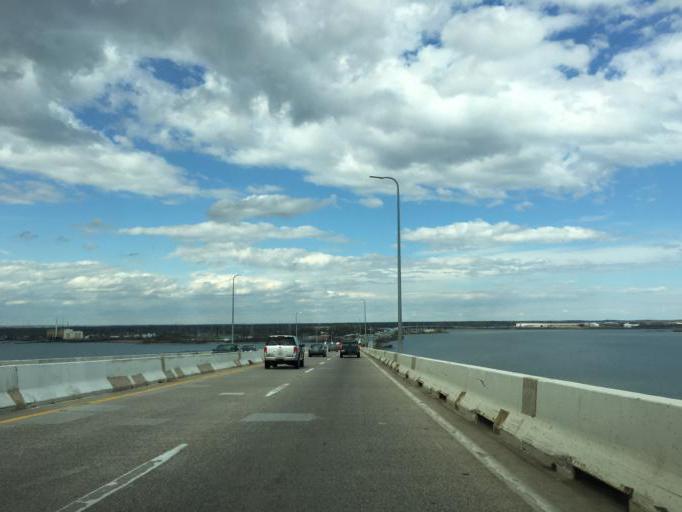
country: US
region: Maryland
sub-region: Baltimore County
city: Dundalk
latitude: 39.2202
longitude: -76.5242
